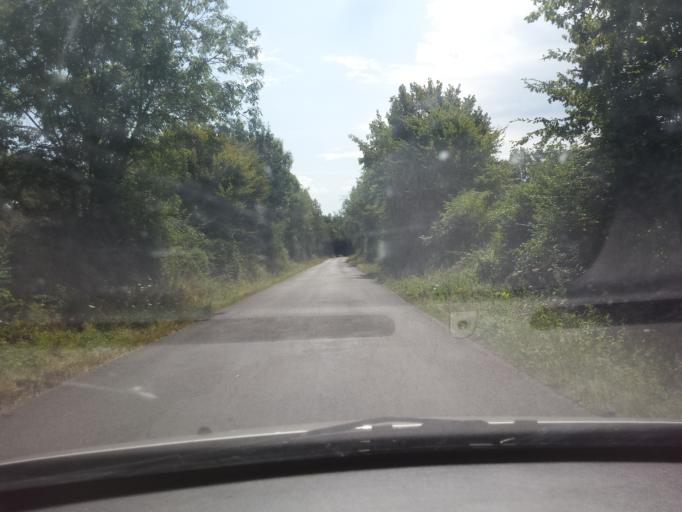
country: FR
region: Poitou-Charentes
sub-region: Departement de la Vienne
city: Availles-Limouzine
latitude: 46.1177
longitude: 0.6704
